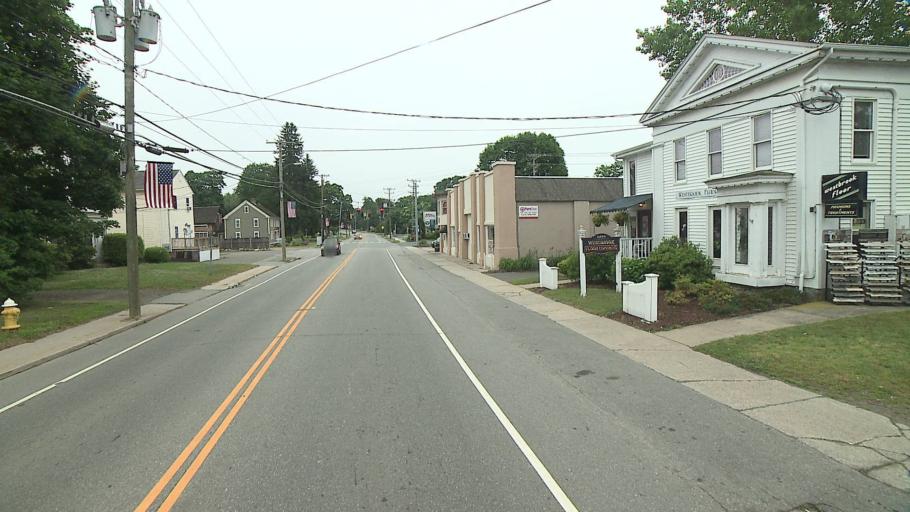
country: US
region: Connecticut
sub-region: Middlesex County
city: Westbrook Center
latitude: 41.2848
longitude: -72.4463
